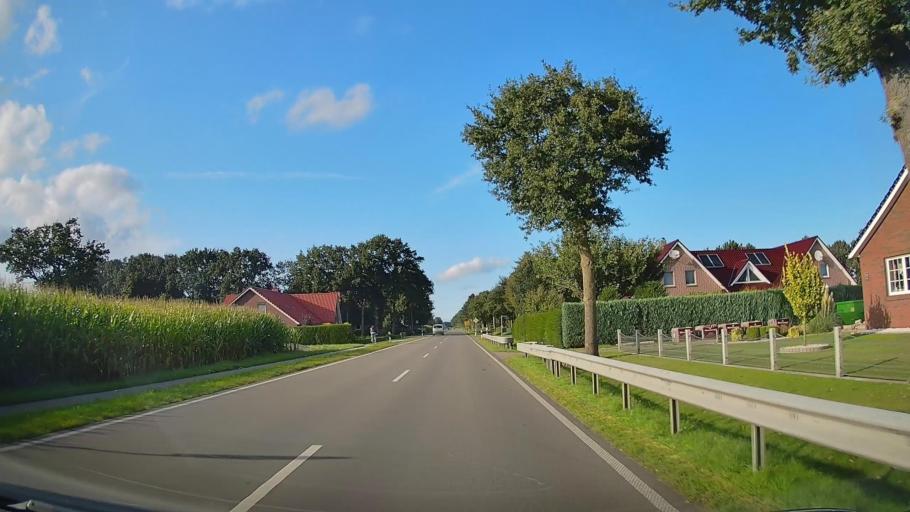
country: DE
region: Lower Saxony
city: Barssel
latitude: 53.0945
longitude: 7.7121
